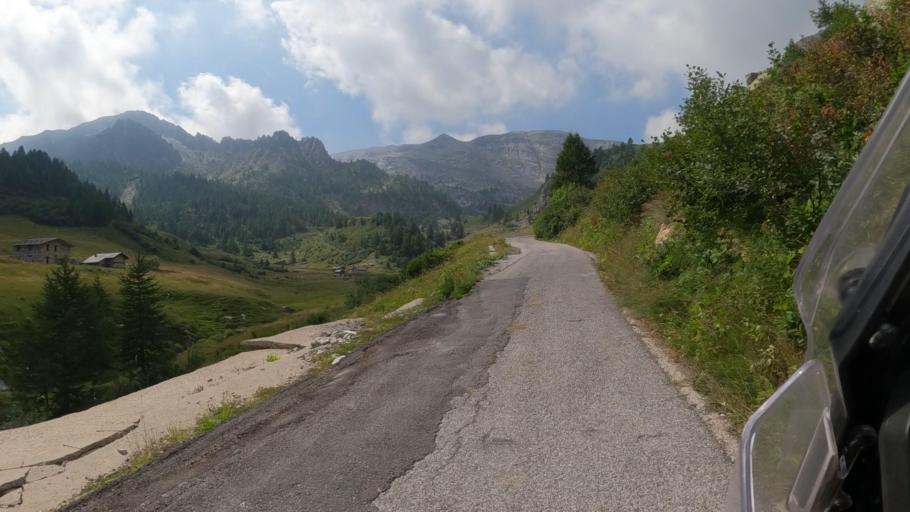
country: IT
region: Piedmont
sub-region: Provincia di Cuneo
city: Marmora
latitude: 44.4041
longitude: 7.1076
